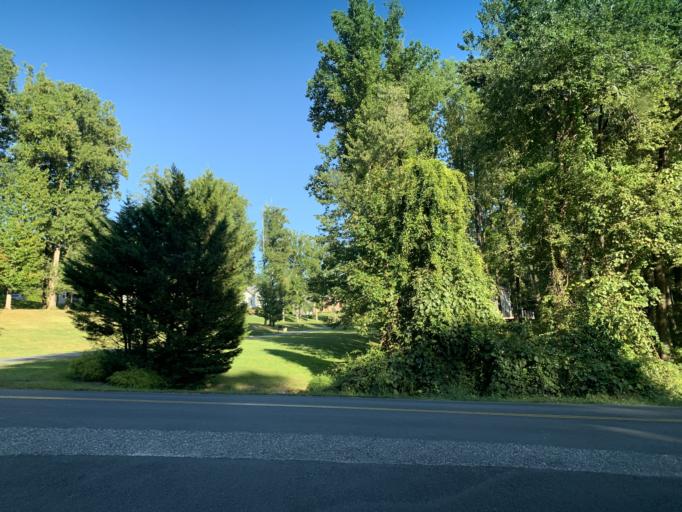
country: US
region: Maryland
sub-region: Harford County
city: Jarrettsville
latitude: 39.5823
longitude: -76.4555
